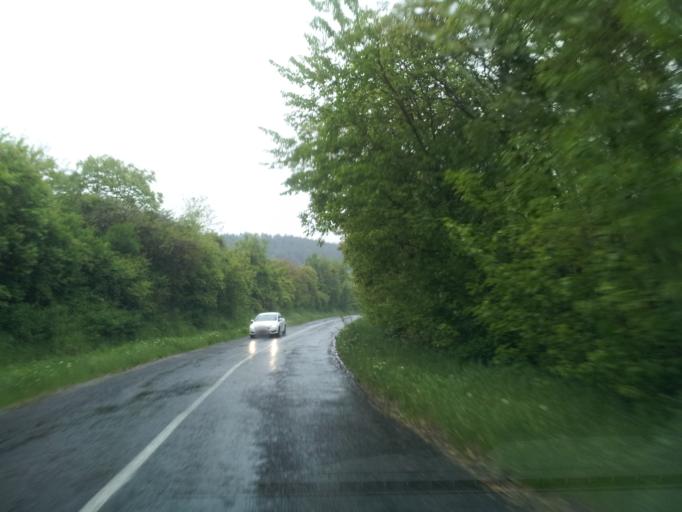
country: HU
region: Tolna
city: Szekszard
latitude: 46.2940
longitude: 18.6770
